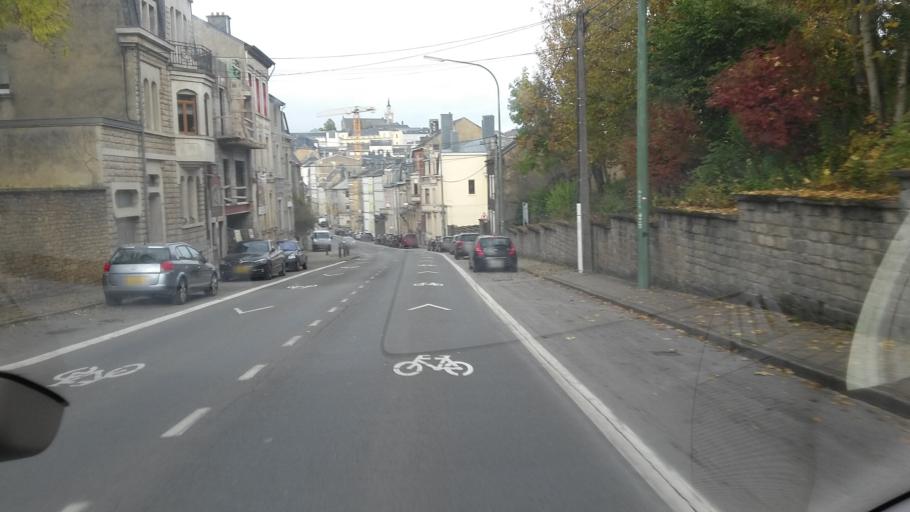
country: BE
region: Wallonia
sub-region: Province du Luxembourg
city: Arlon
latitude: 49.6796
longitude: 5.8208
